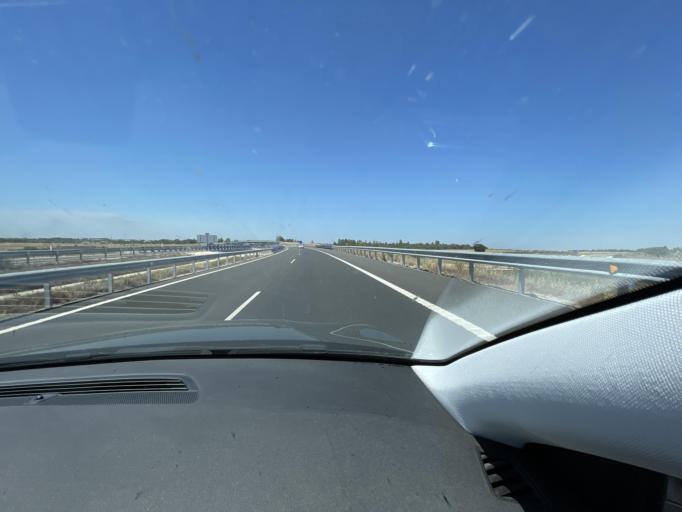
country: ES
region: Castille and Leon
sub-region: Provincia de Salamanca
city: Fuentes de Onoro
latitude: 40.6122
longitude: -6.8177
